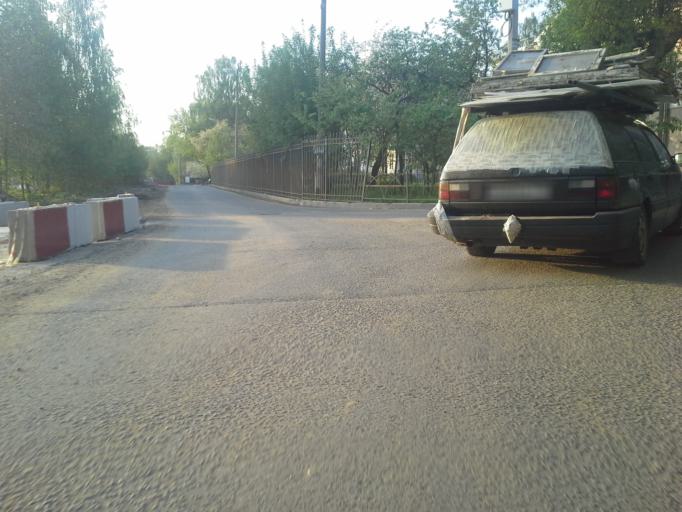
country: RU
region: Moskovskaya
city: Kommunarka
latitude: 55.5605
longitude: 37.4736
